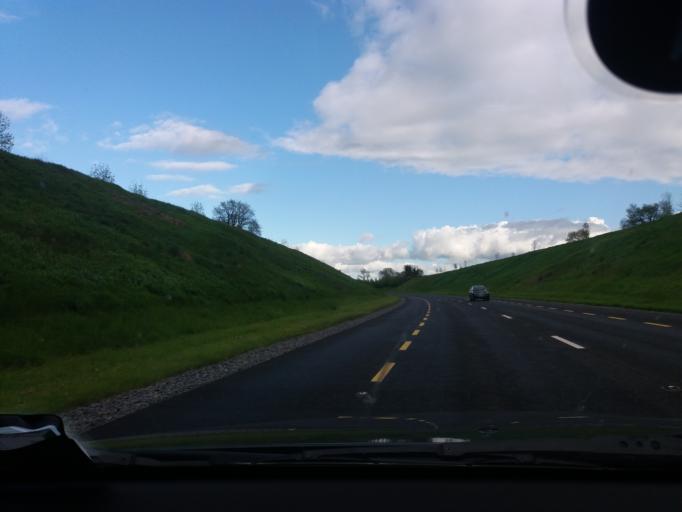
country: IE
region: Leinster
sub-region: Kilkenny
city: Kilkenny
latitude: 52.6465
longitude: -7.1879
